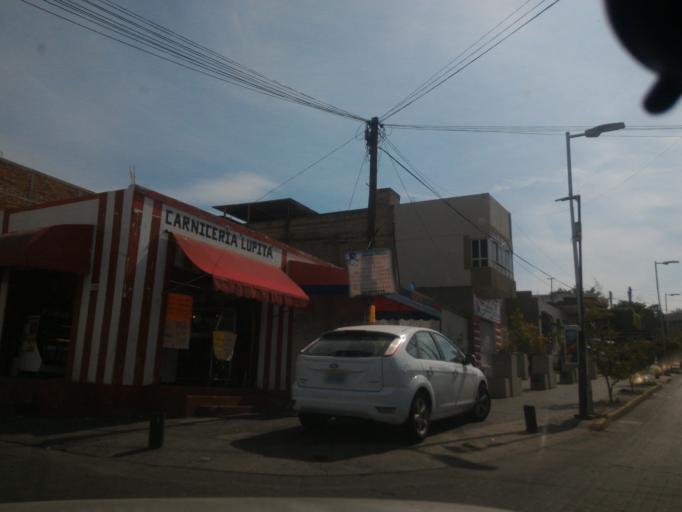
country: MX
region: Jalisco
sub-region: Tlajomulco de Zuniga
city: Altus Bosques
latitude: 20.6140
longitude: -103.3815
